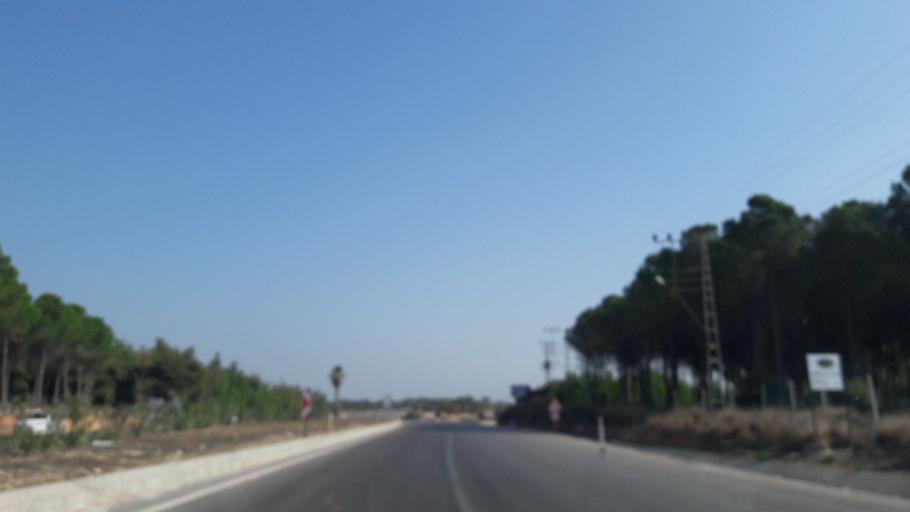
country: TR
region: Adana
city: Yakapinar
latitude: 37.1179
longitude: 35.5144
